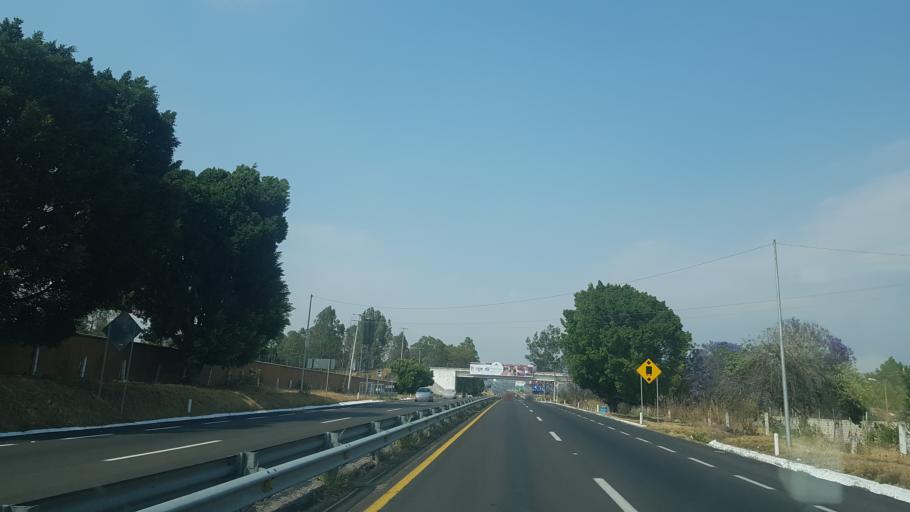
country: MX
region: Puebla
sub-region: Atlixco
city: San Agustin Huixaxtla
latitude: 18.9271
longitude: -98.3987
